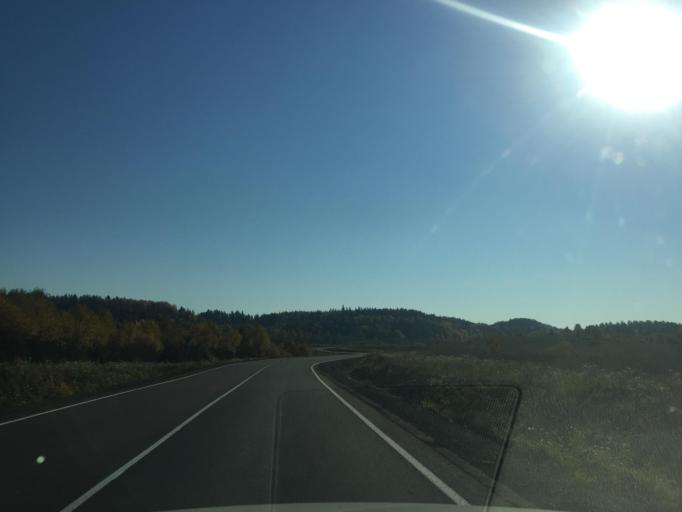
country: RU
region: Leningrad
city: Kuznechnoye
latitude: 61.3383
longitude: 29.8608
